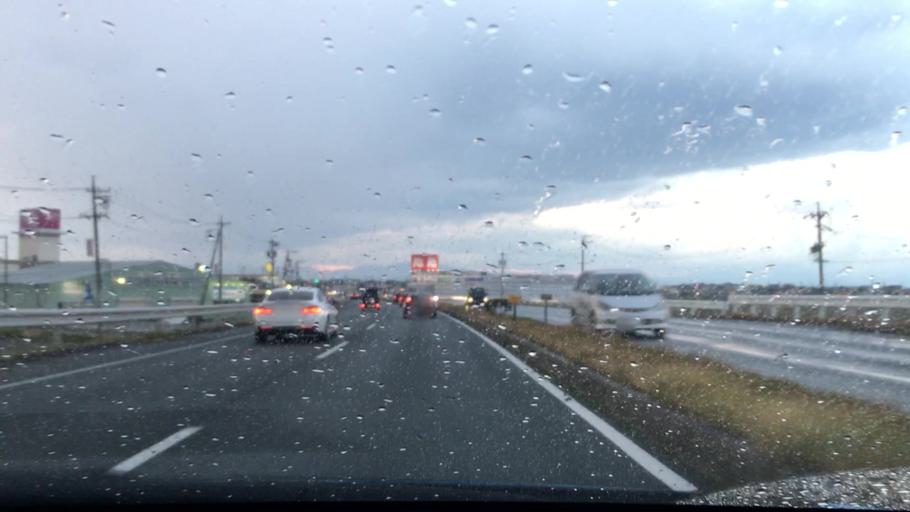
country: JP
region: Mie
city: Ise
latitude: 34.5801
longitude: 136.6204
